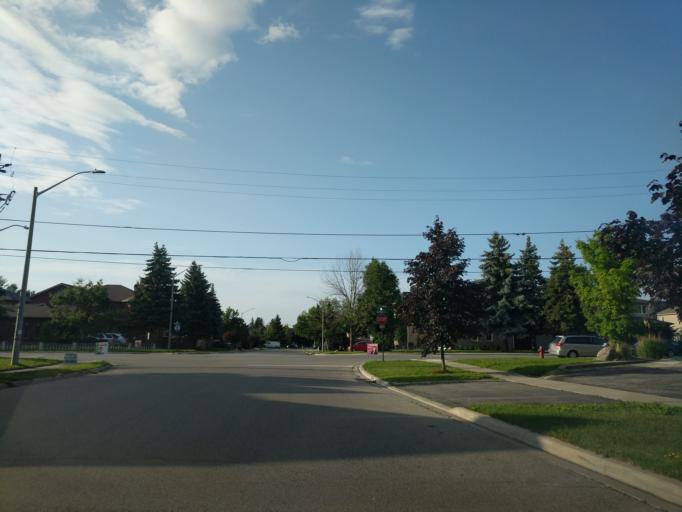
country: CA
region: Ontario
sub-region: York
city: Richmond Hill
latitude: 43.8982
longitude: -79.4473
